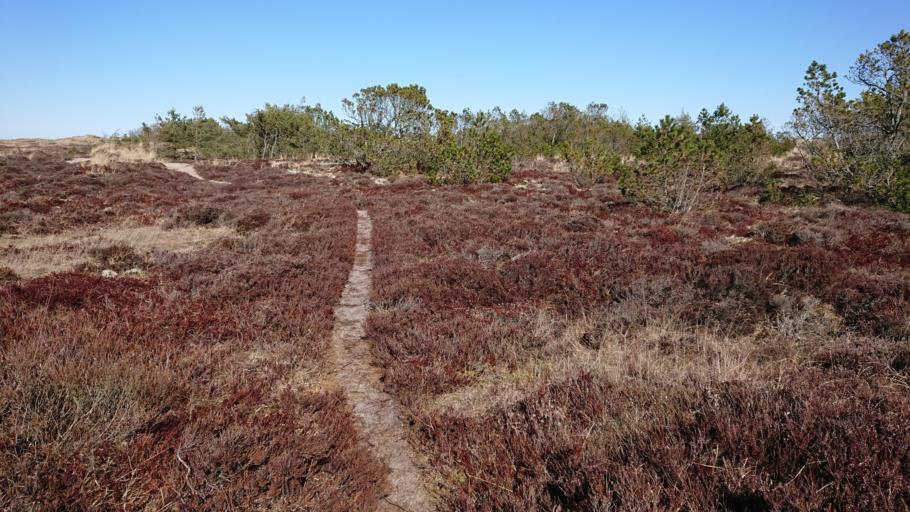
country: DK
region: North Denmark
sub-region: Frederikshavn Kommune
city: Strandby
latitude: 57.6307
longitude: 10.3567
